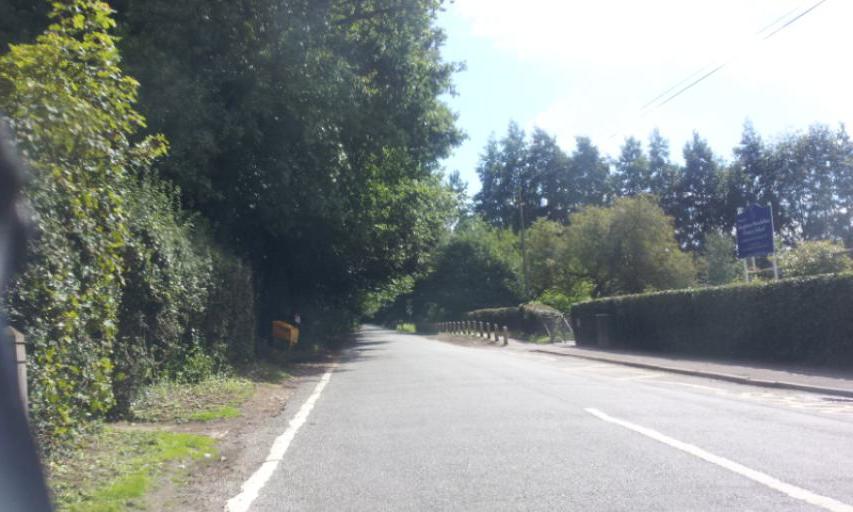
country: GB
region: England
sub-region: Kent
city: Maidstone
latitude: 51.2291
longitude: 0.5327
